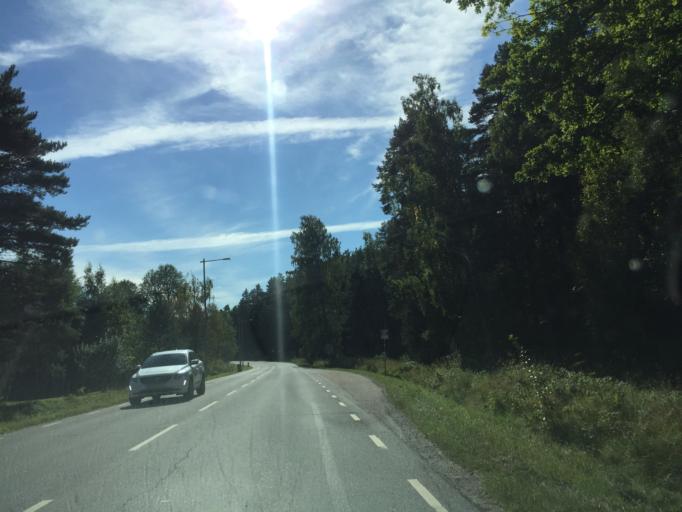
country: SE
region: OErebro
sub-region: Orebro Kommun
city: Orebro
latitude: 59.2949
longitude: 15.2501
